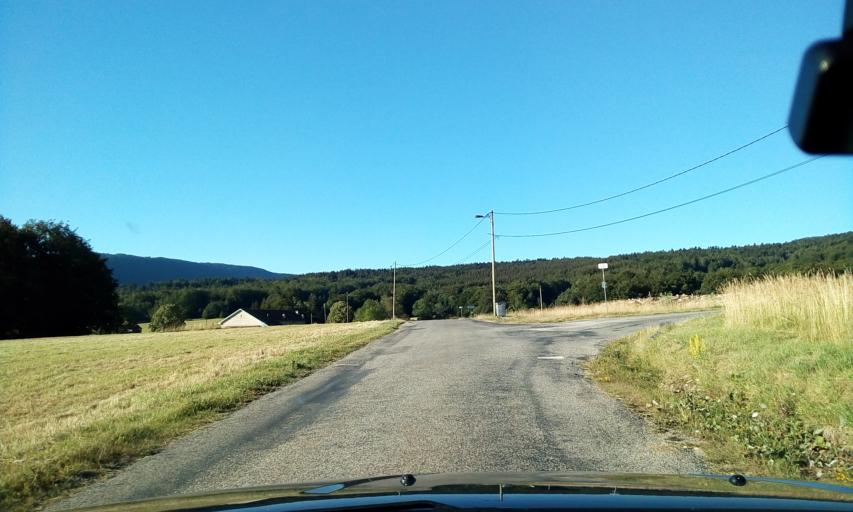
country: FR
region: Rhone-Alpes
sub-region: Departement de la Drome
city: Die
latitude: 44.8709
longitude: 5.3610
